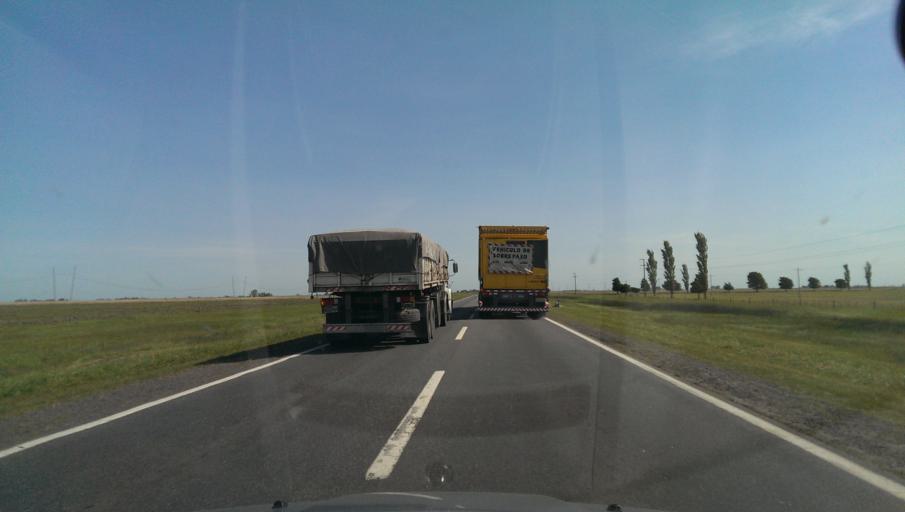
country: AR
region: Buenos Aires
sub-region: Partido de Azul
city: Azul
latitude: -36.6175
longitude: -59.6855
